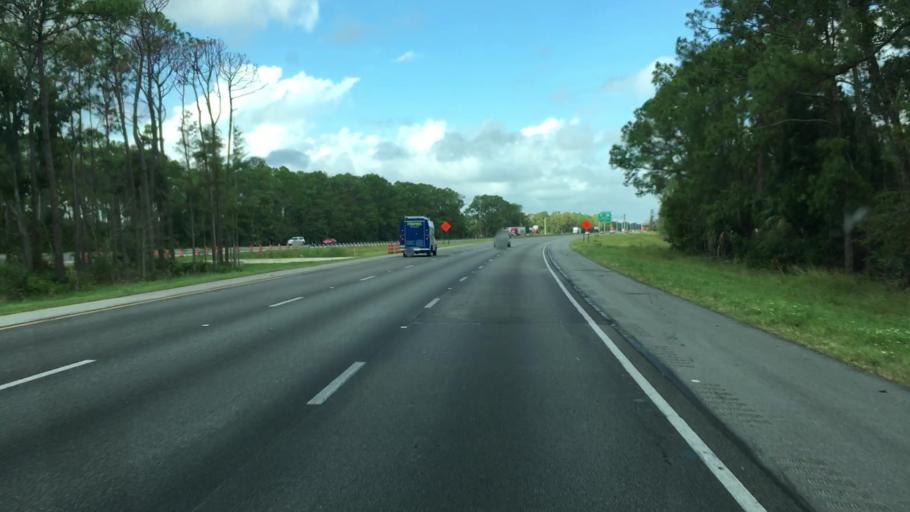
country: US
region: Florida
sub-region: Volusia County
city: South Daytona
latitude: 29.1322
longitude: -81.0617
